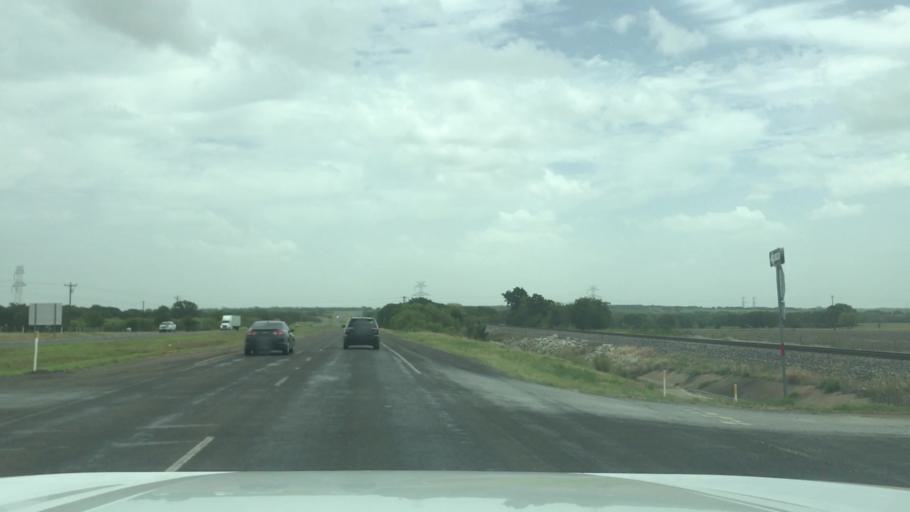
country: US
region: Texas
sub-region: McLennan County
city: Riesel
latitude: 31.5101
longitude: -96.9516
